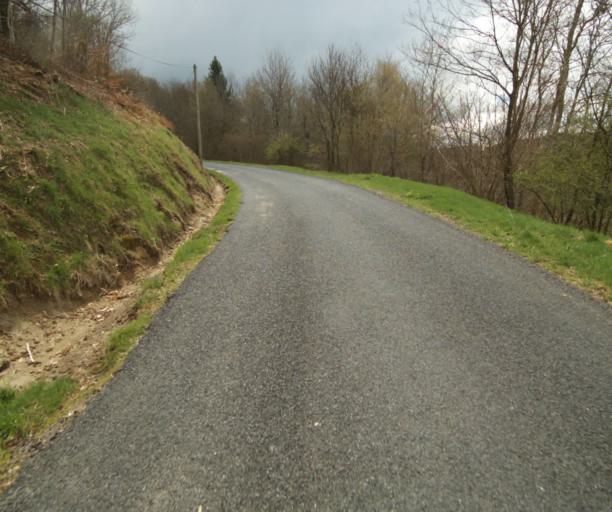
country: FR
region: Limousin
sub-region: Departement de la Correze
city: Laguenne
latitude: 45.2494
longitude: 1.8881
